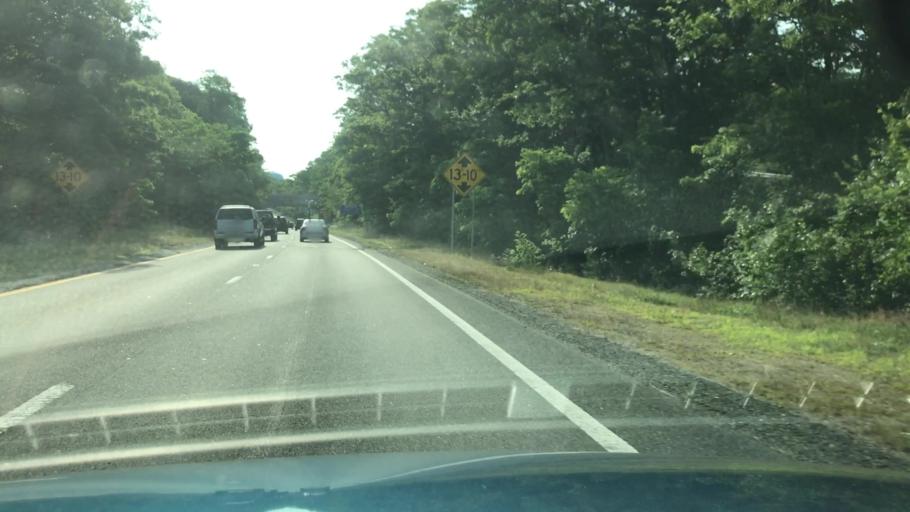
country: US
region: Massachusetts
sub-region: Barnstable County
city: West Barnstable
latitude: 41.6841
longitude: -70.3560
